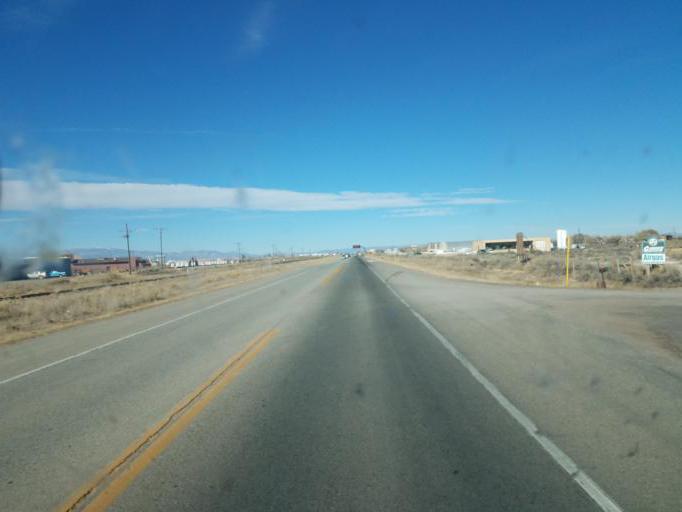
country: US
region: Colorado
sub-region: Alamosa County
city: Alamosa
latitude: 37.4848
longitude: -105.9173
